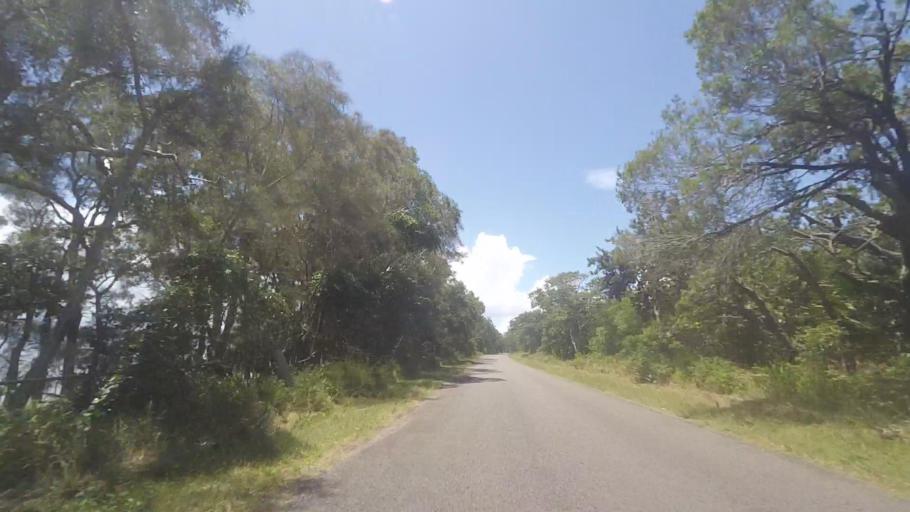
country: AU
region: New South Wales
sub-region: Great Lakes
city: Bulahdelah
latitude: -32.5344
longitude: 152.3205
